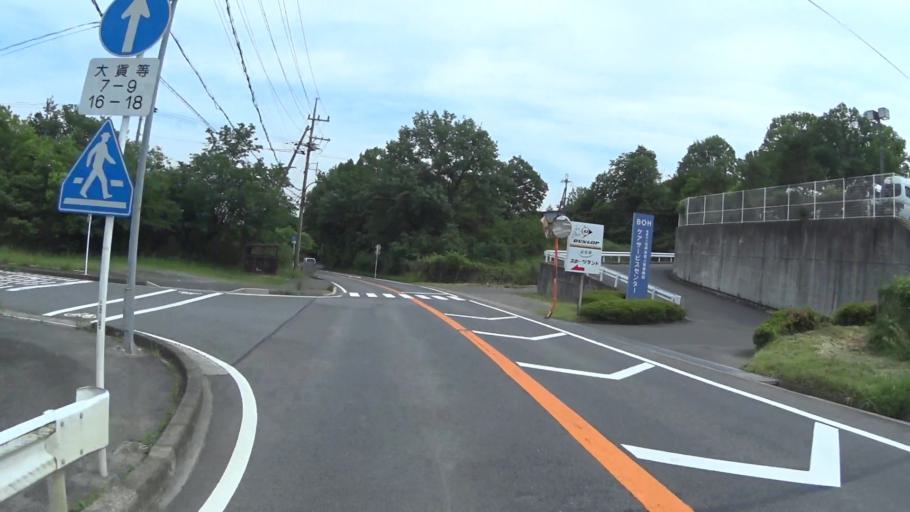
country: JP
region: Shiga Prefecture
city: Kitahama
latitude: 35.1563
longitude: 135.8760
